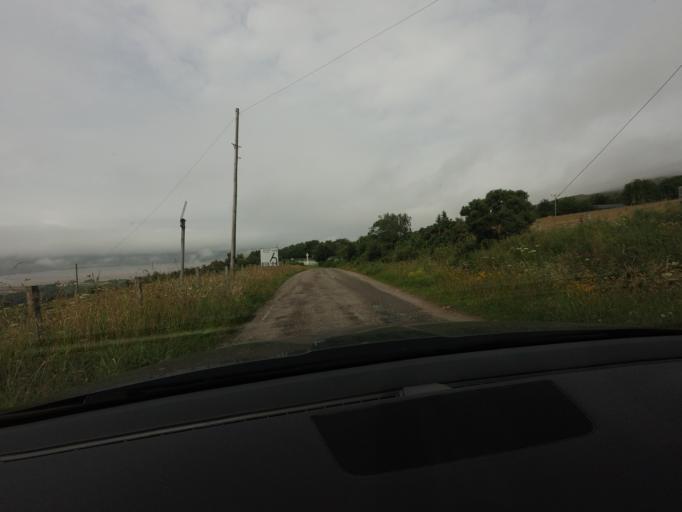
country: GB
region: Scotland
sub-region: Highland
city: Golspie
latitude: 58.4857
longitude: -4.4128
